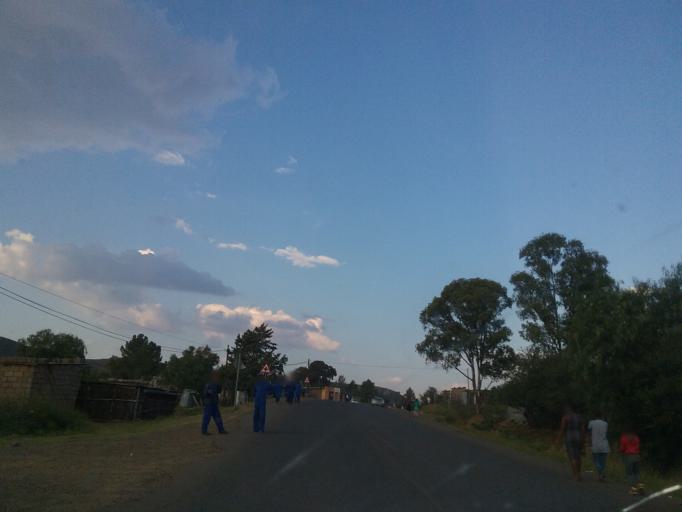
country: LS
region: Quthing
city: Quthing
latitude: -30.3975
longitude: 27.6638
